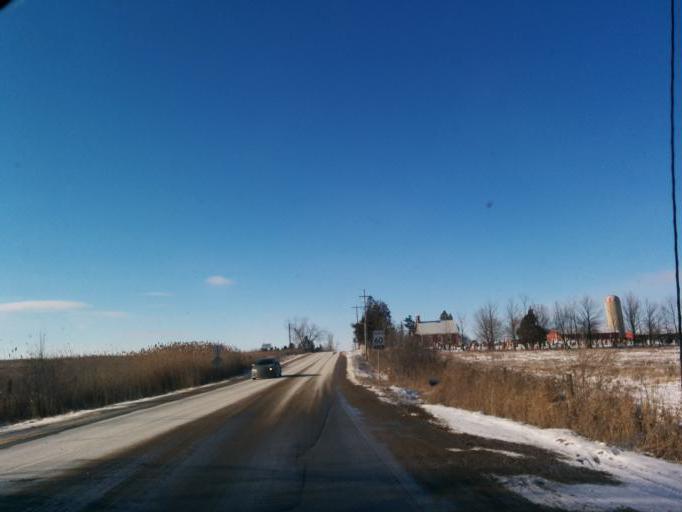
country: CA
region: Ontario
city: Brampton
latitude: 43.7594
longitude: -79.8357
